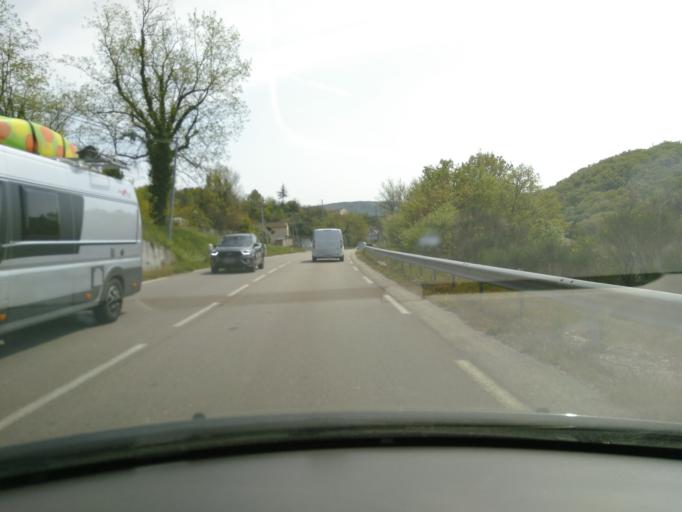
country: FR
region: Rhone-Alpes
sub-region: Departement de l'Ardeche
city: Le Teil
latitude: 44.5506
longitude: 4.6606
